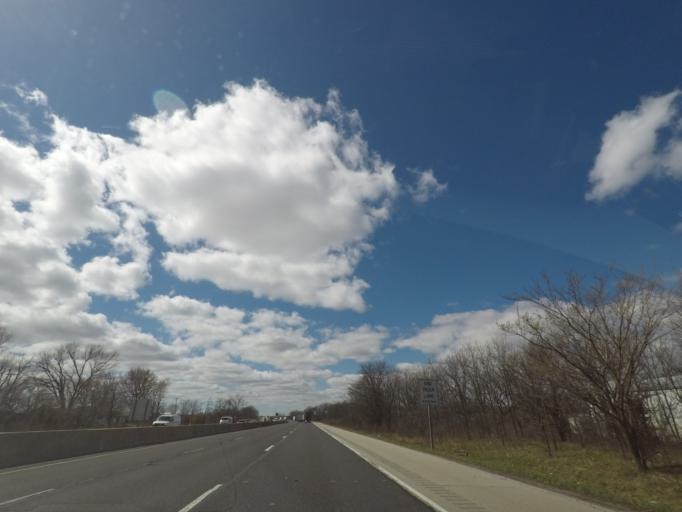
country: US
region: Illinois
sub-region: Will County
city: Shorewood
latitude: 41.5131
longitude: -88.1950
